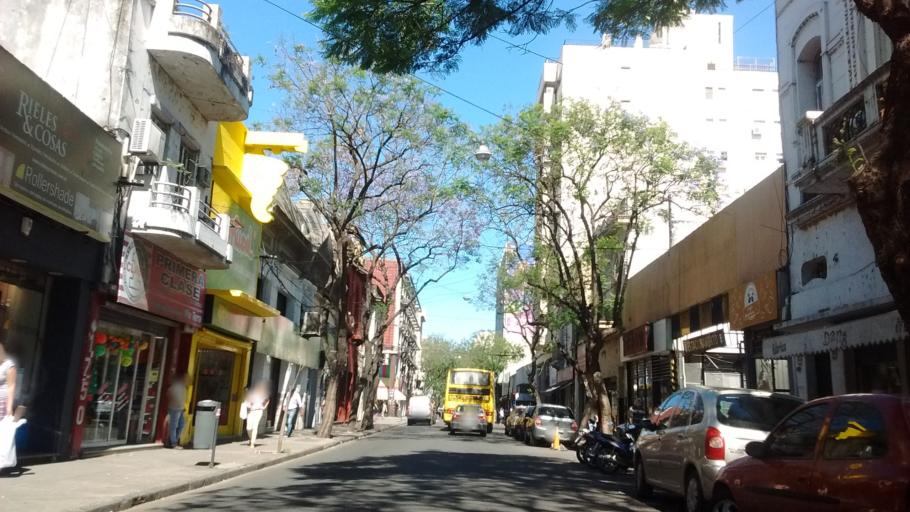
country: AR
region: Santa Fe
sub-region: Departamento de Rosario
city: Rosario
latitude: -32.9474
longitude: -60.6480
